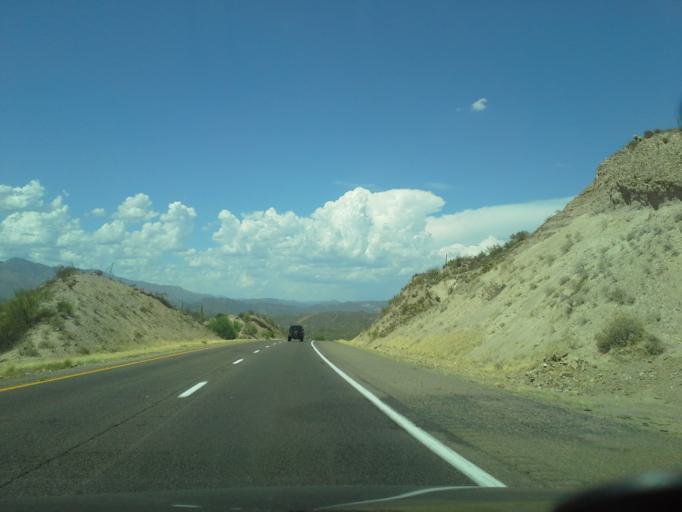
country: US
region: Arizona
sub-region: Maricopa County
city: New River
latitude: 33.9871
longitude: -112.1334
